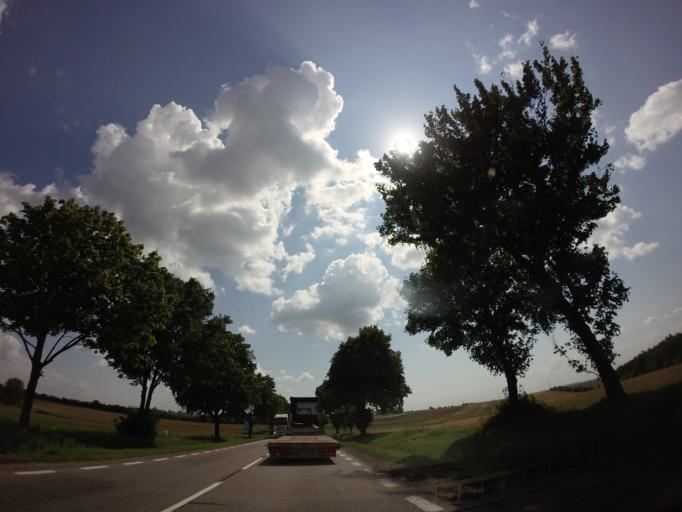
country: PL
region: Podlasie
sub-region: Powiat lomzynski
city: Piatnica
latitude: 53.2172
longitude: 22.1066
